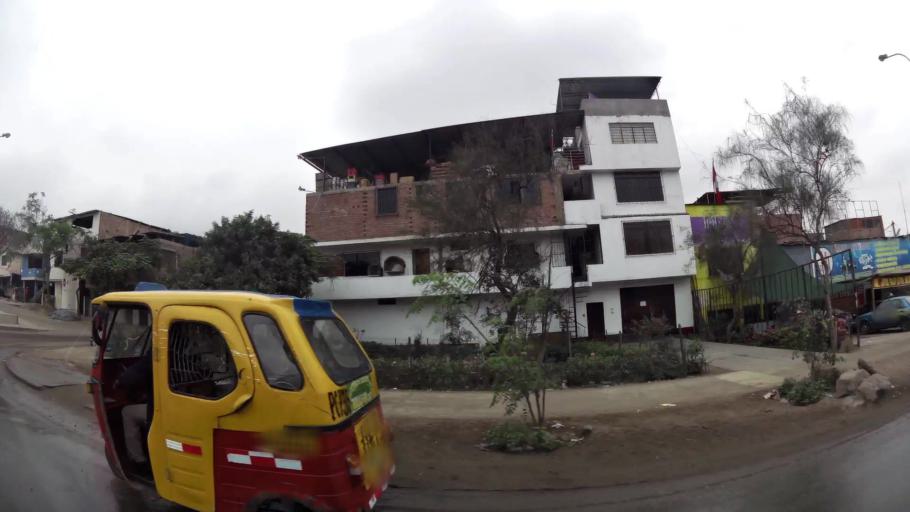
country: PE
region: Lima
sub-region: Lima
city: Surco
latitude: -12.1435
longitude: -76.9645
